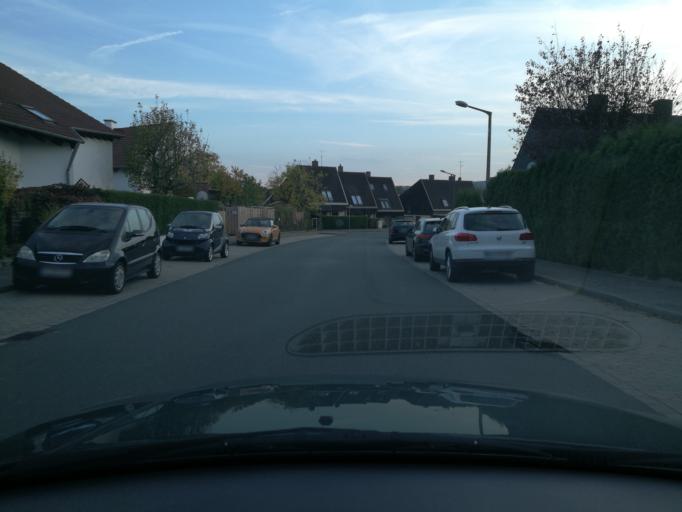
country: DE
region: Bavaria
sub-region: Regierungsbezirk Mittelfranken
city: Zirndorf
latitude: 49.4901
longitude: 10.9390
